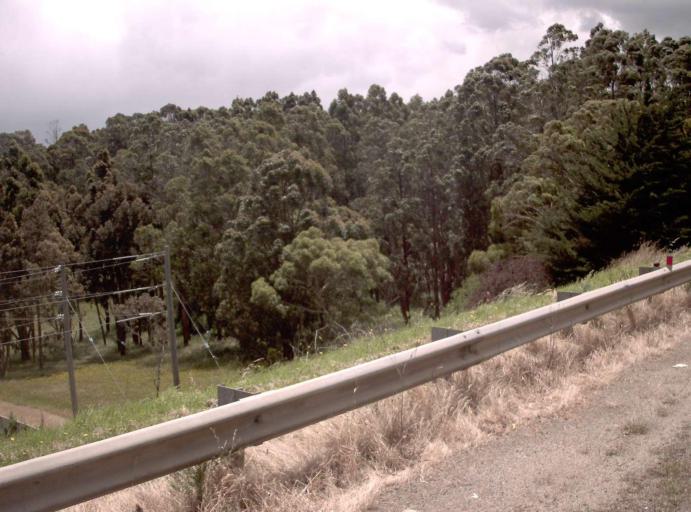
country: AU
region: Victoria
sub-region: Baw Baw
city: Warragul
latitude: -38.1414
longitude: 145.8806
